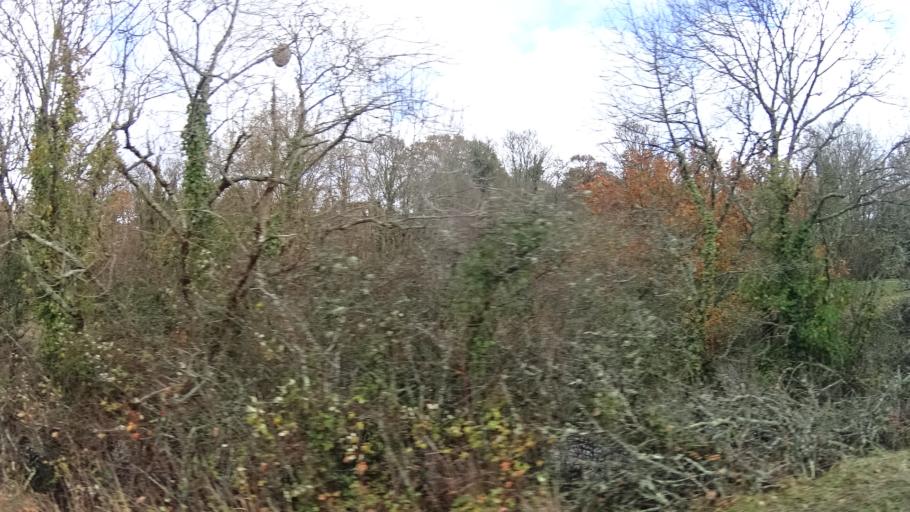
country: FR
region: Brittany
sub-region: Departement du Morbihan
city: Rieux
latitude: 47.5974
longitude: -2.0908
